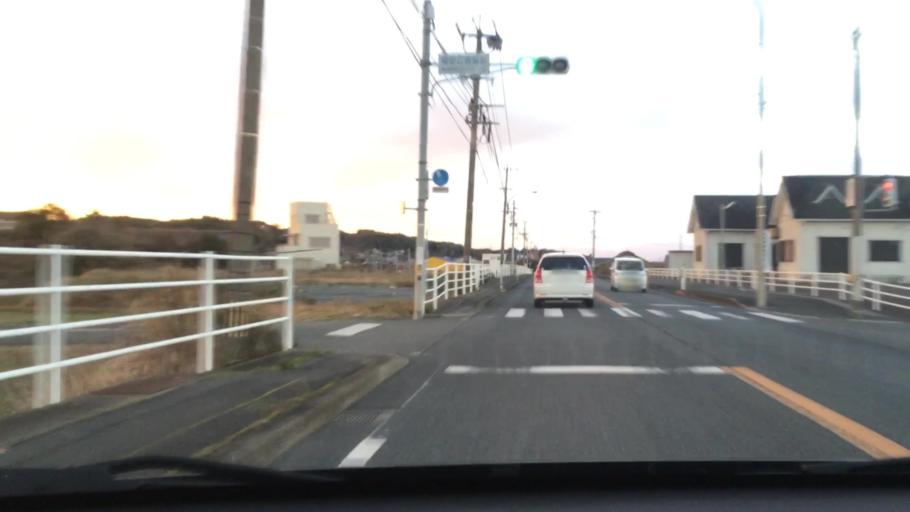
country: JP
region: Fukuoka
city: Shiida
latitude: 33.6303
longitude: 131.0842
